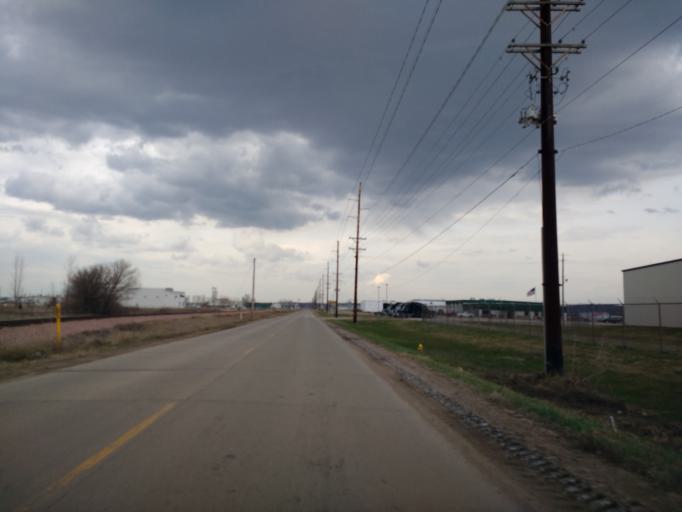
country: US
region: Iowa
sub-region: Woodbury County
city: Sergeant Bluff
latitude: 42.4103
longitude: -96.3700
